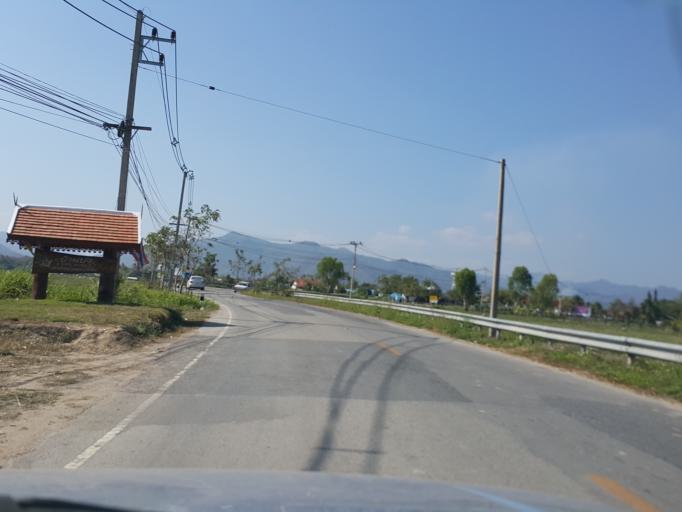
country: TH
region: Chiang Mai
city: Mae Wang
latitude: 18.6016
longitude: 98.8003
